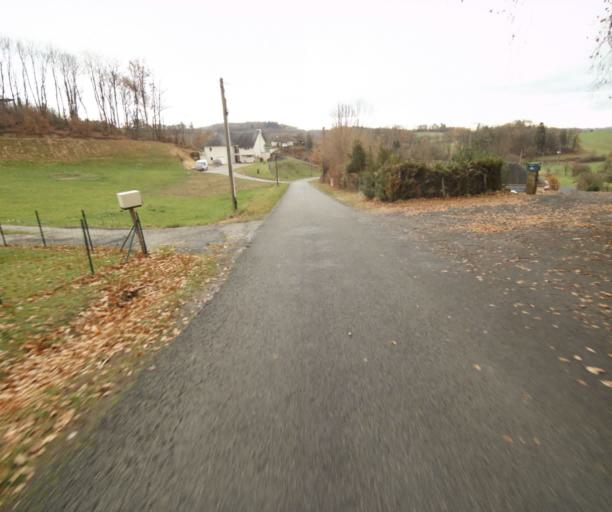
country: FR
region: Limousin
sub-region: Departement de la Correze
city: Saint-Mexant
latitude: 45.2890
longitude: 1.6335
